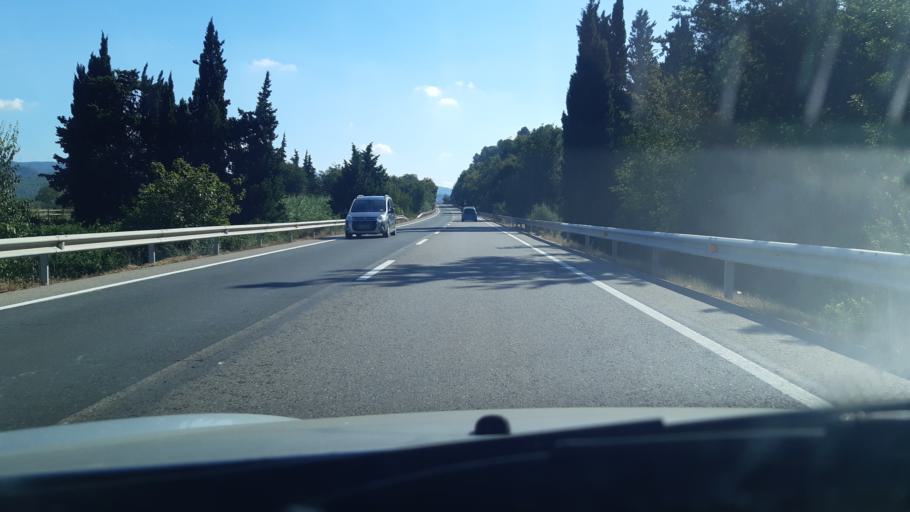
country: ES
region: Catalonia
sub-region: Provincia de Tarragona
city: Tivenys
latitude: 40.8658
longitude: 0.5053
